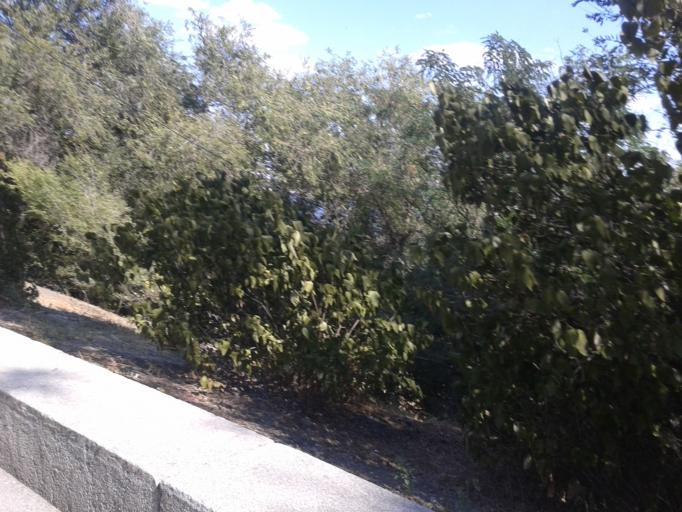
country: RU
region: Volgograd
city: Volgograd
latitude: 48.7074
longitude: 44.5259
